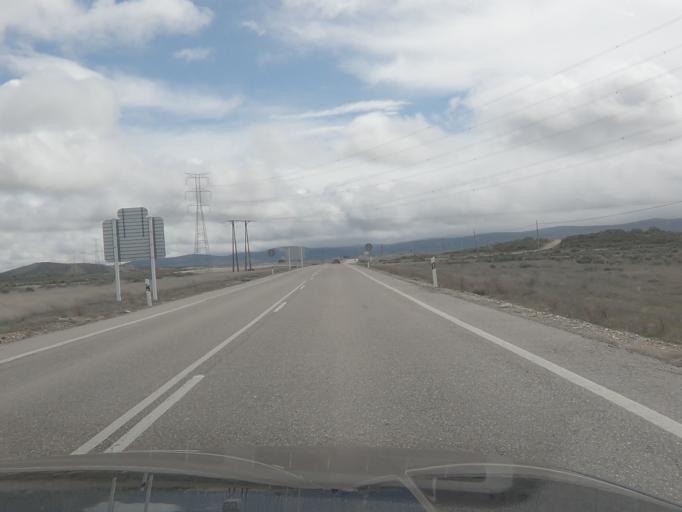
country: ES
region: Castille and Leon
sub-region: Provincia de Zamora
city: Villardeciervos
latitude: 41.9976
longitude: -6.2481
